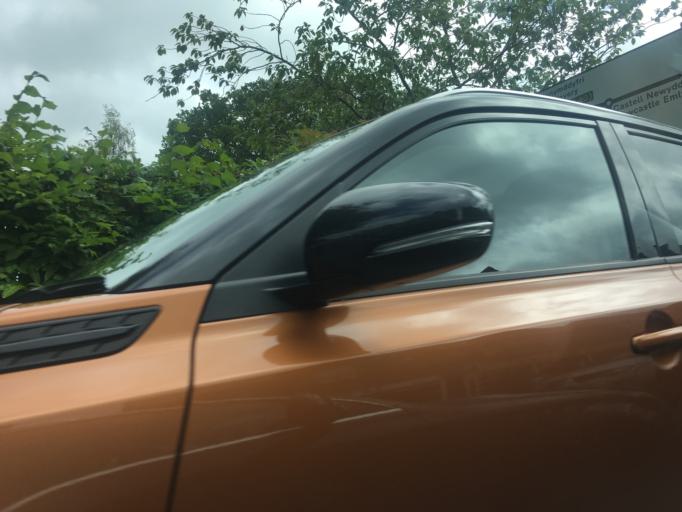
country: GB
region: Wales
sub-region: County of Ceredigion
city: Lampeter
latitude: 52.1138
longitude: -4.0777
